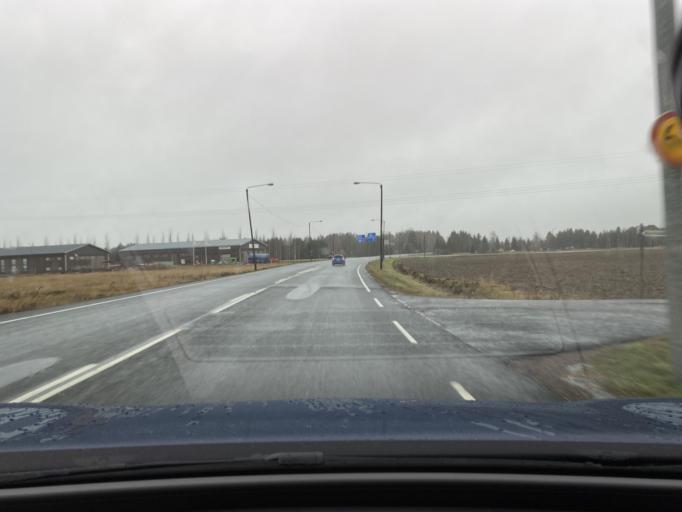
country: FI
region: Varsinais-Suomi
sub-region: Loimaa
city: Loimaa
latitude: 60.8681
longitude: 23.0066
